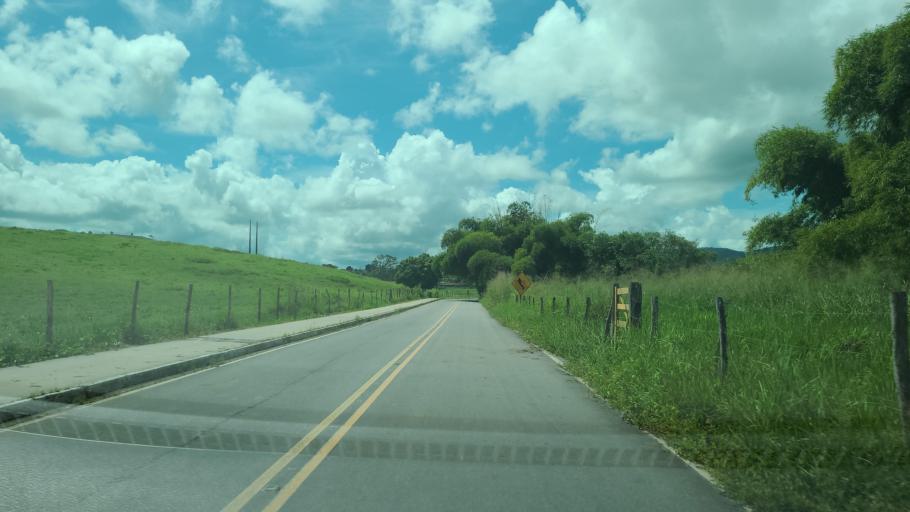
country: BR
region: Alagoas
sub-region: Uniao Dos Palmares
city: Uniao dos Palmares
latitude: -9.1572
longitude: -36.0422
